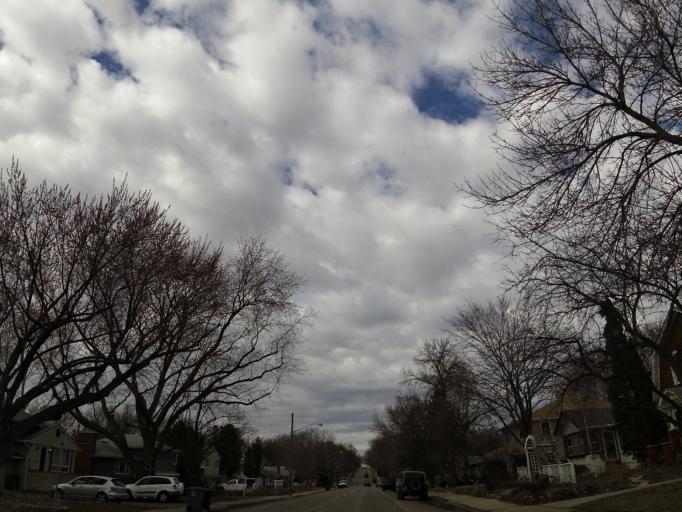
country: US
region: Minnesota
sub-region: Hennepin County
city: Edina
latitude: 44.9161
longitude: -93.3189
